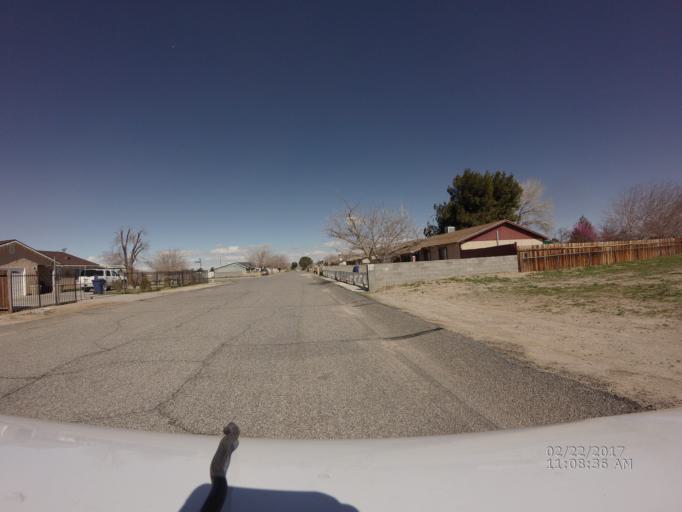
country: US
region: California
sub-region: Los Angeles County
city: Lake Los Angeles
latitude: 34.6273
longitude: -117.8168
